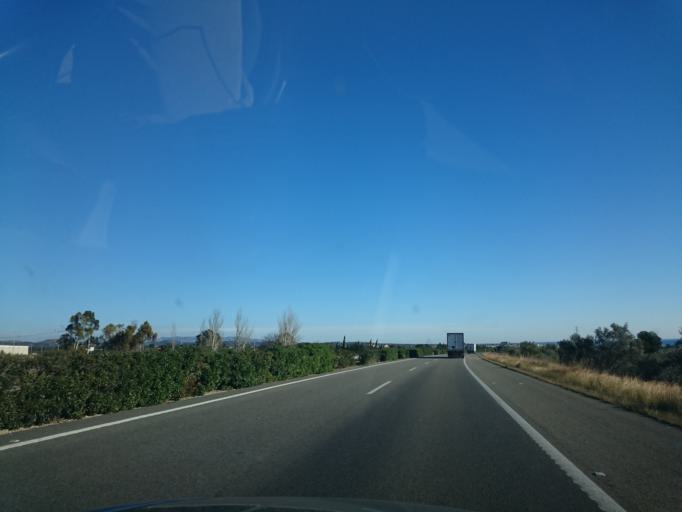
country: ES
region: Catalonia
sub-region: Provincia de Tarragona
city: Camarles
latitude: 40.8005
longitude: 0.6745
